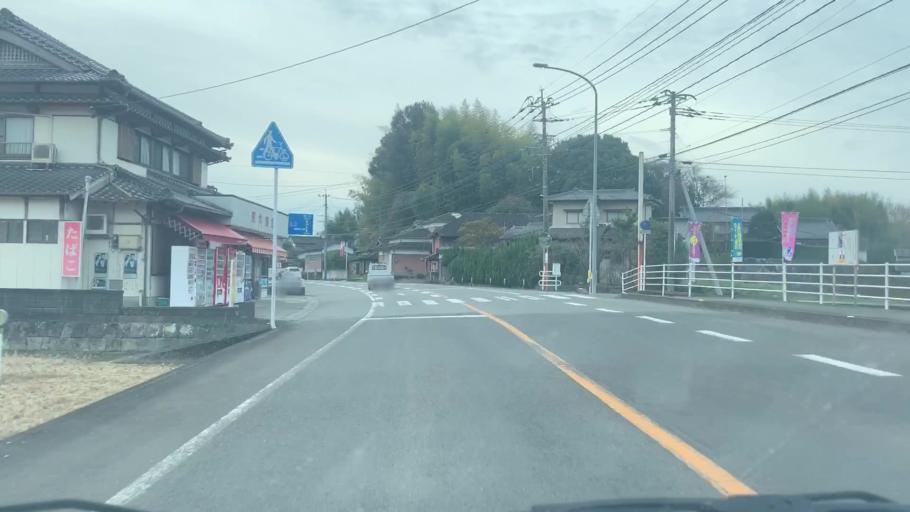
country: JP
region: Saga Prefecture
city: Kashima
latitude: 33.1405
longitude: 130.0637
